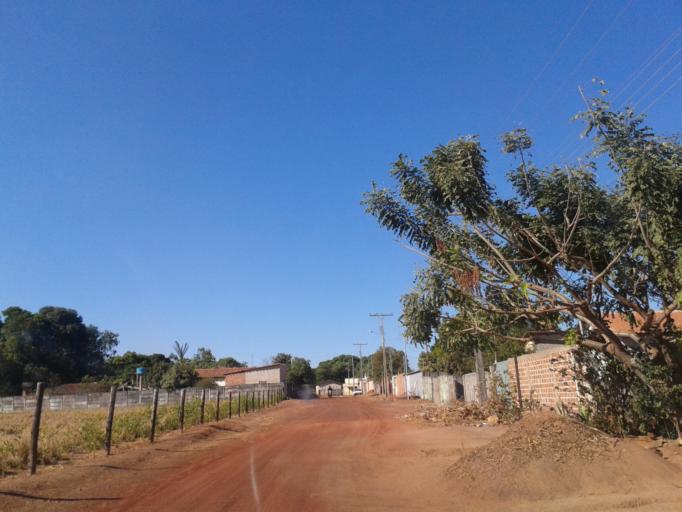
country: BR
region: Goias
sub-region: Sao Miguel Do Araguaia
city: Sao Miguel do Araguaia
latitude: -13.2850
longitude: -50.1778
